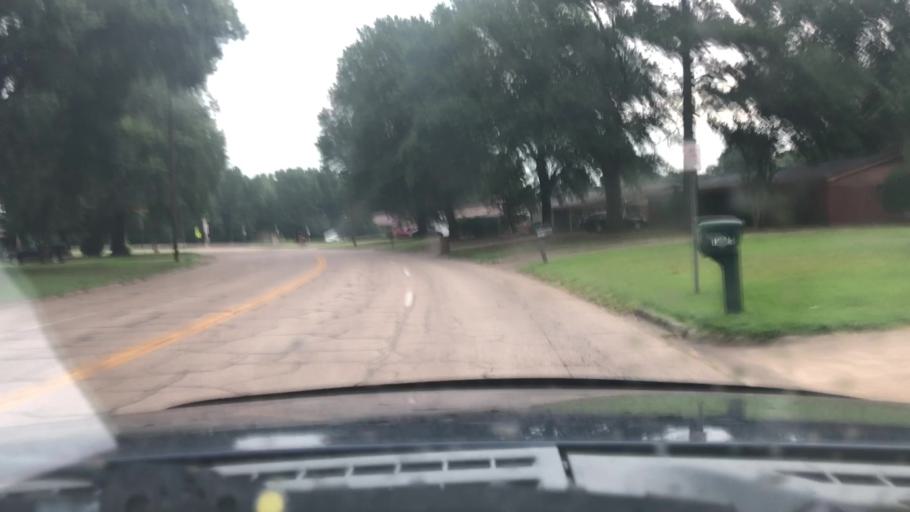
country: US
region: Texas
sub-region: Bowie County
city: Wake Village
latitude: 33.4043
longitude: -94.0793
